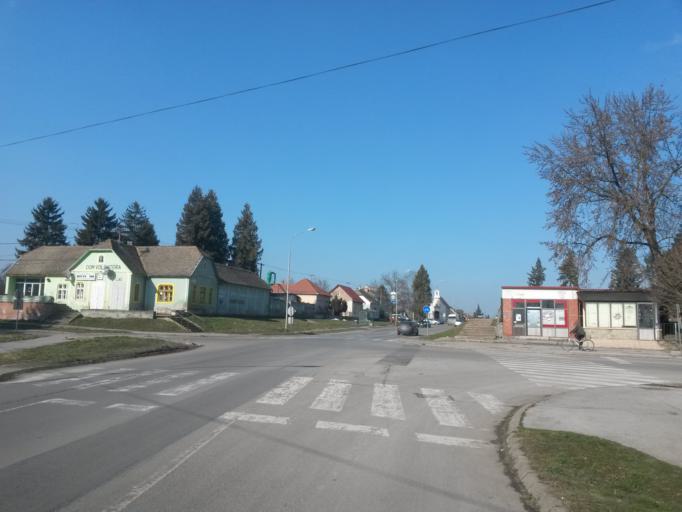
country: HR
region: Osjecko-Baranjska
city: Valpovo
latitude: 45.6653
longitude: 18.4153
